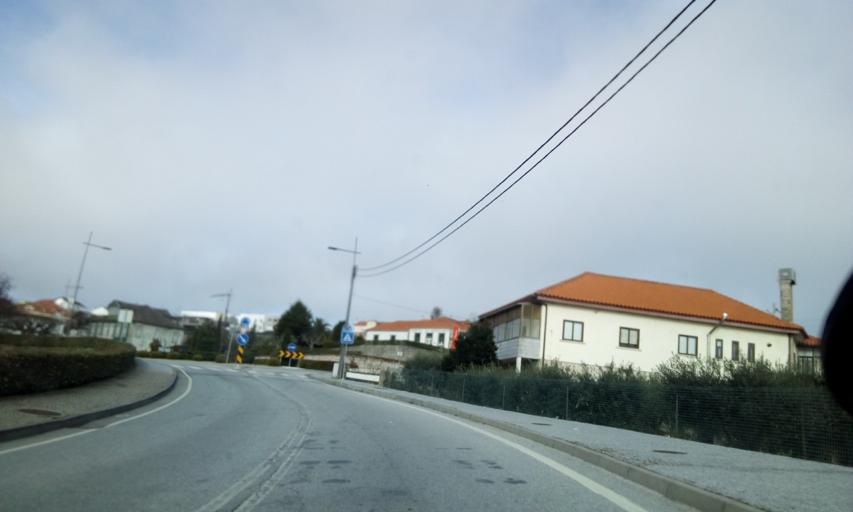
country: PT
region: Guarda
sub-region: Aguiar da Beira
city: Aguiar da Beira
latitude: 40.8187
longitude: -7.5391
